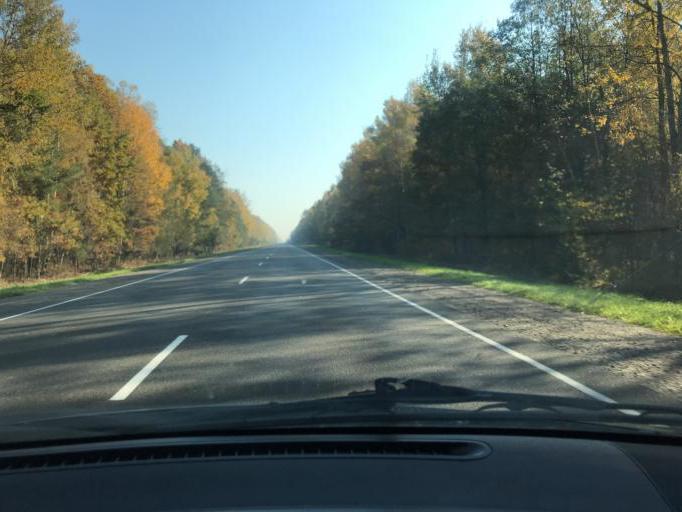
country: BY
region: Brest
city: Horad Luninyets
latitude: 52.3067
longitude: 26.6903
